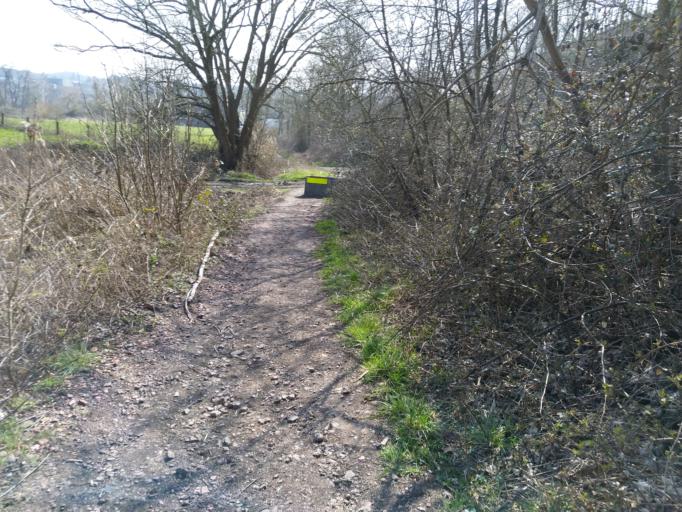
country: BE
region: Wallonia
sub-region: Province du Hainaut
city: Chasse Royale
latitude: 50.4319
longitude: 3.9426
